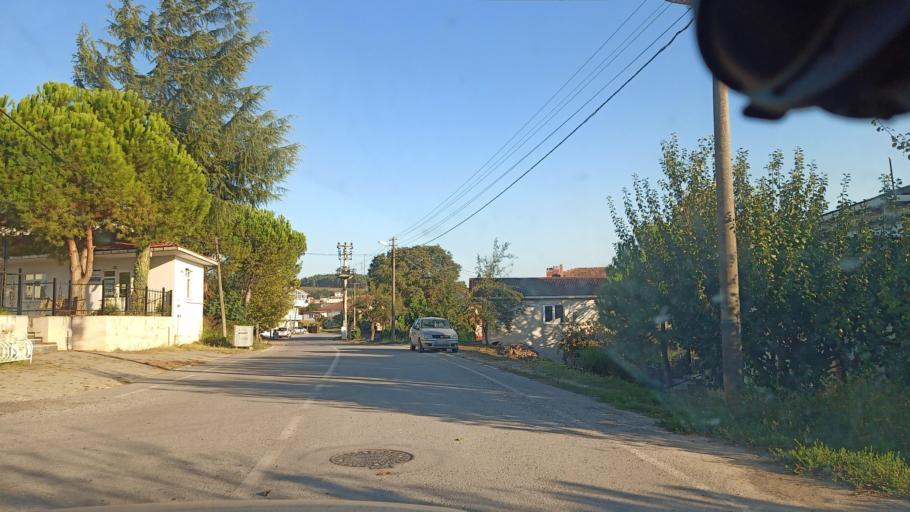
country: TR
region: Sakarya
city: Ferizli
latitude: 40.9464
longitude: 30.4829
